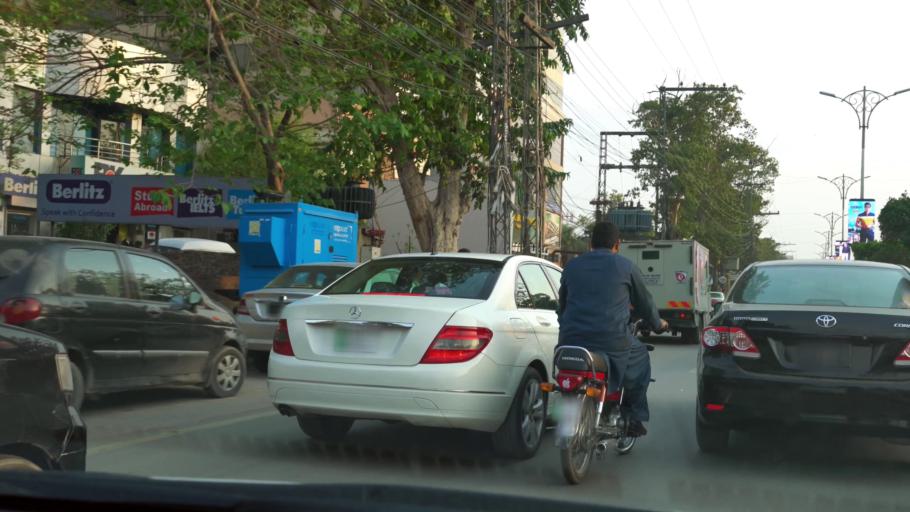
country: PK
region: Punjab
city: Lahore
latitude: 31.5118
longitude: 74.3510
